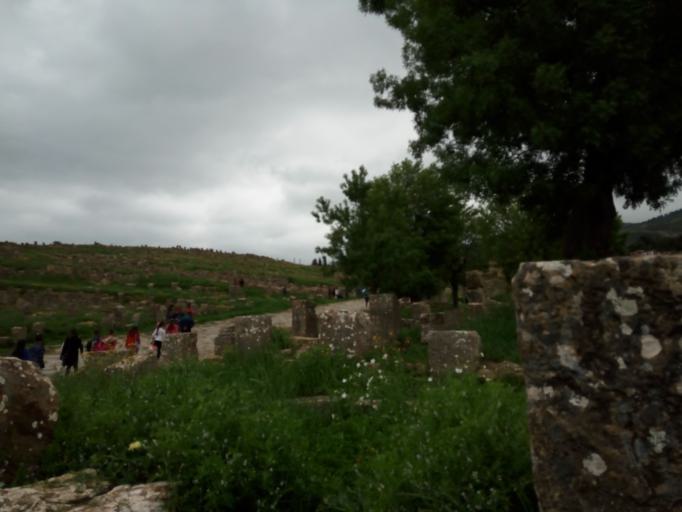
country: DZ
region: Setif
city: El Eulma
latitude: 36.3202
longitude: 5.7357
